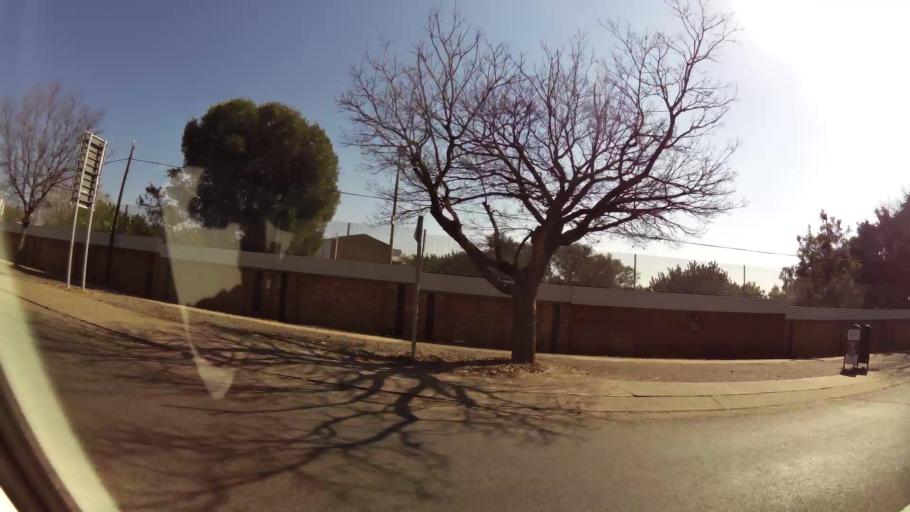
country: ZA
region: Gauteng
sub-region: City of Tshwane Metropolitan Municipality
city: Pretoria
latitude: -25.7660
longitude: 28.2595
